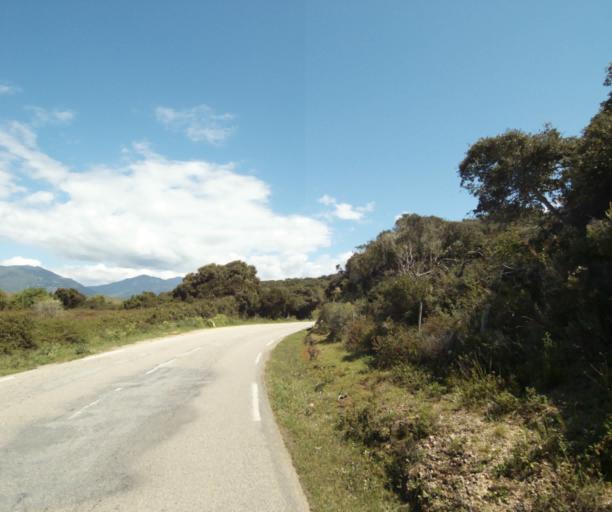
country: FR
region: Corsica
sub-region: Departement de la Corse-du-Sud
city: Propriano
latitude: 41.6492
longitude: 8.8782
